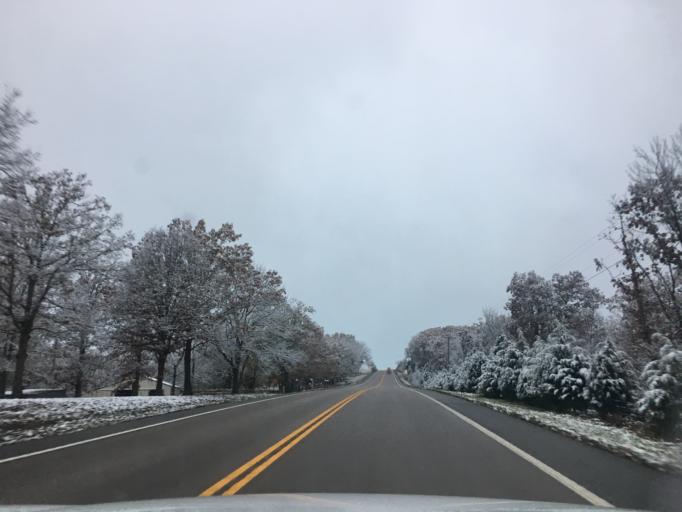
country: US
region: Missouri
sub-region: Osage County
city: Linn
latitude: 38.4716
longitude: -91.7803
